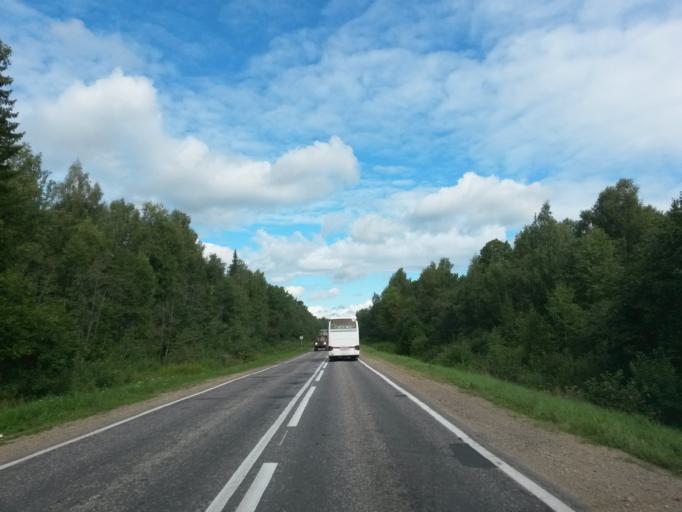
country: RU
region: Jaroslavl
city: Krasnyye Tkachi
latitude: 57.4745
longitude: 39.9076
